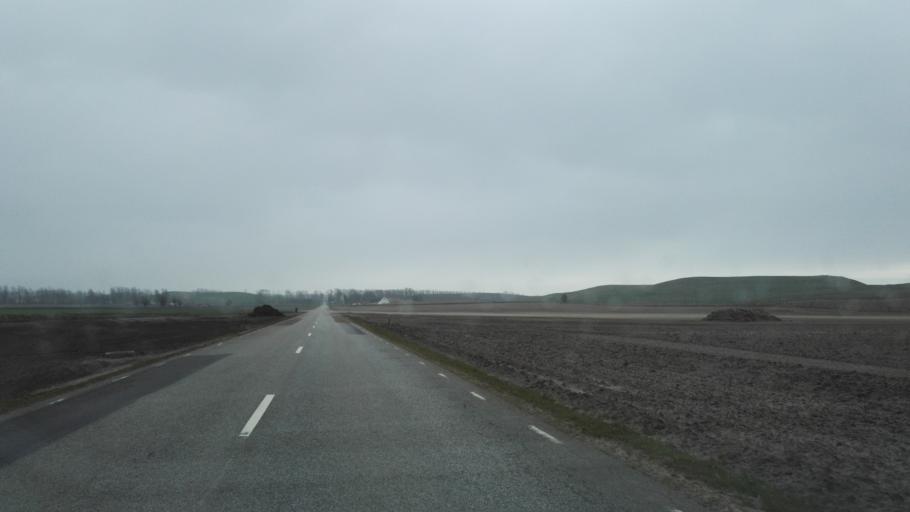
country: SE
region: Skane
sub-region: Ystads Kommun
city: Kopingebro
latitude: 55.3977
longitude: 14.0314
